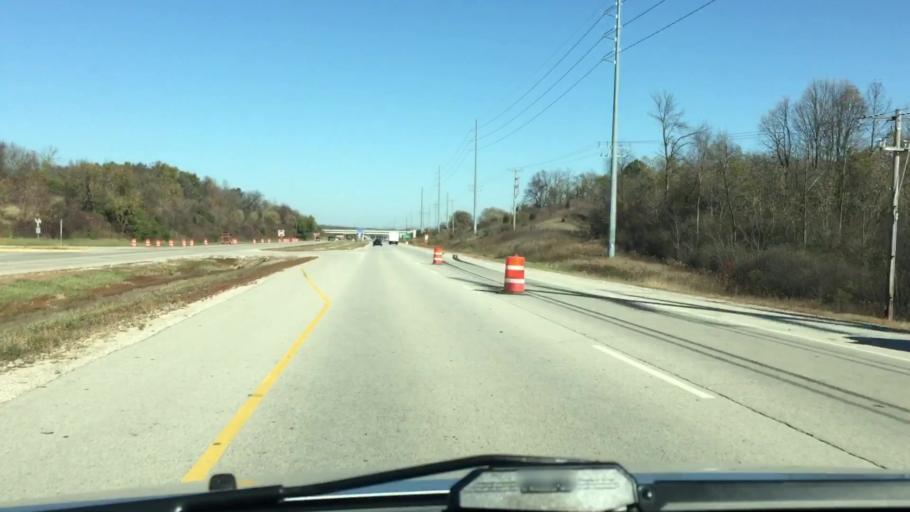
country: US
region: Wisconsin
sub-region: Waukesha County
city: Pewaukee
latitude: 43.0768
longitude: -88.2056
